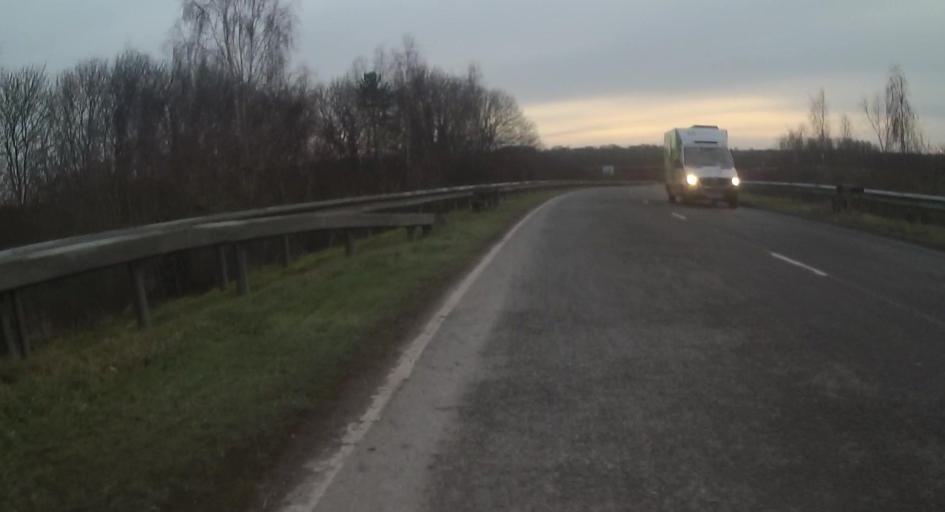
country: GB
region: England
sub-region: Hampshire
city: Kings Worthy
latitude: 51.1803
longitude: -1.3737
